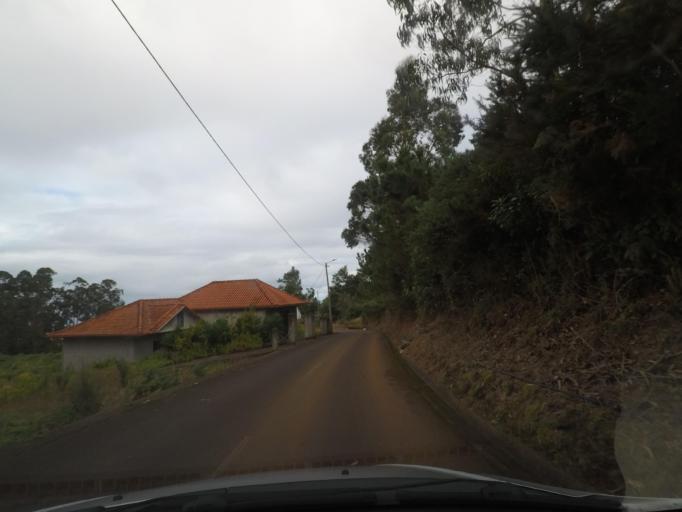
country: PT
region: Madeira
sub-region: Santana
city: Santana
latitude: 32.7818
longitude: -16.8778
